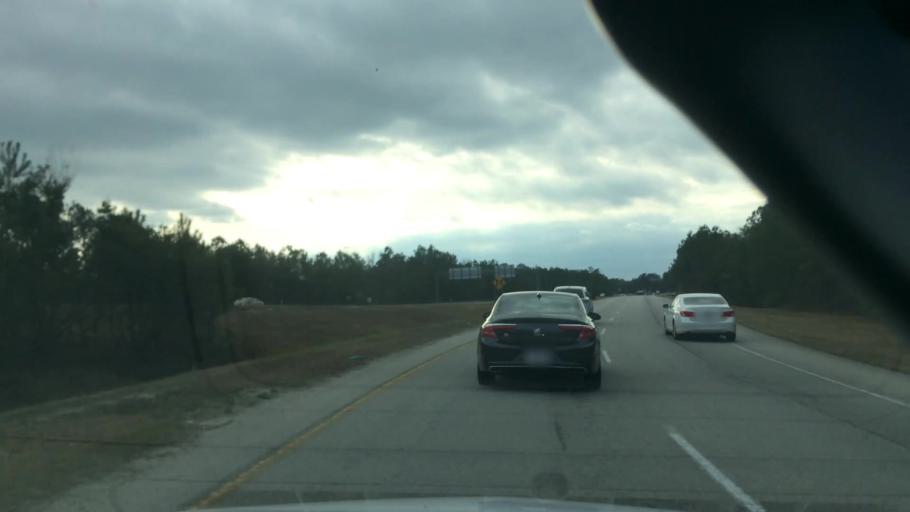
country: US
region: South Carolina
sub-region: Horry County
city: North Myrtle Beach
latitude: 33.8745
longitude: -78.6840
